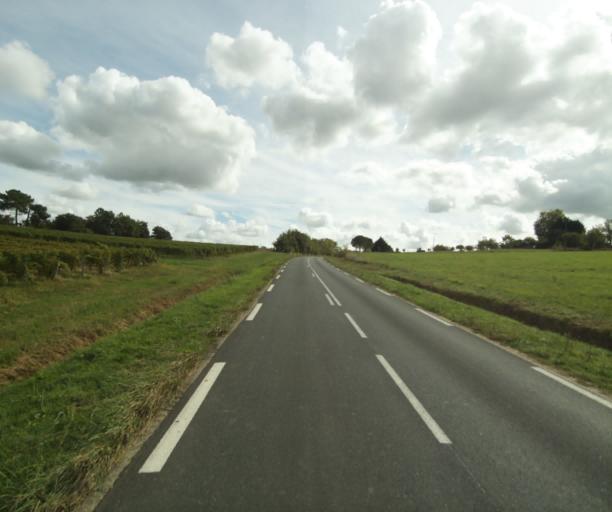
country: FR
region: Midi-Pyrenees
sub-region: Departement du Gers
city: Eauze
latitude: 43.8275
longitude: 0.0940
